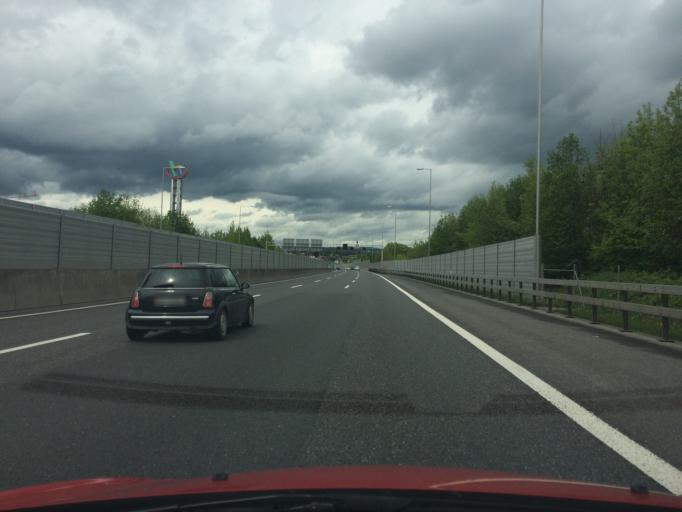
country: CH
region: Lucerne
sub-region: Hochdorf District
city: Emmen
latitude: 47.0728
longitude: 8.2953
